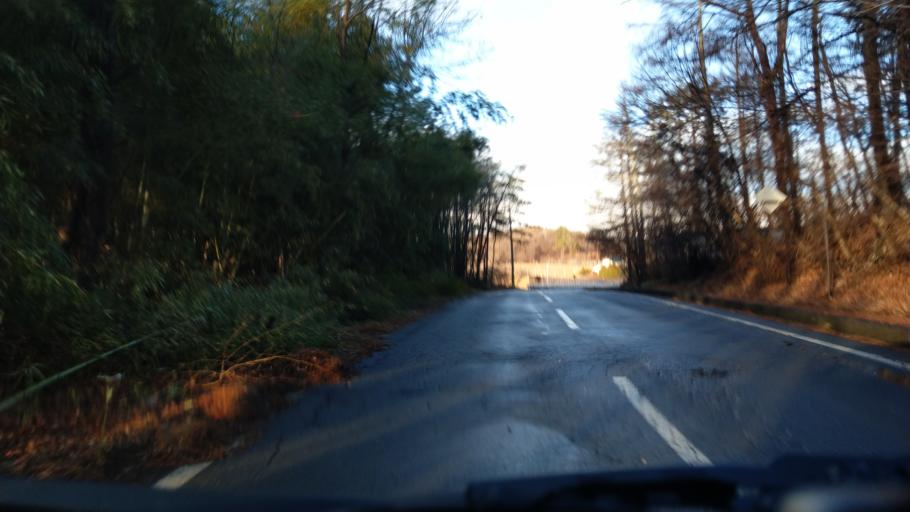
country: JP
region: Nagano
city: Komoro
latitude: 36.3071
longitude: 138.3870
